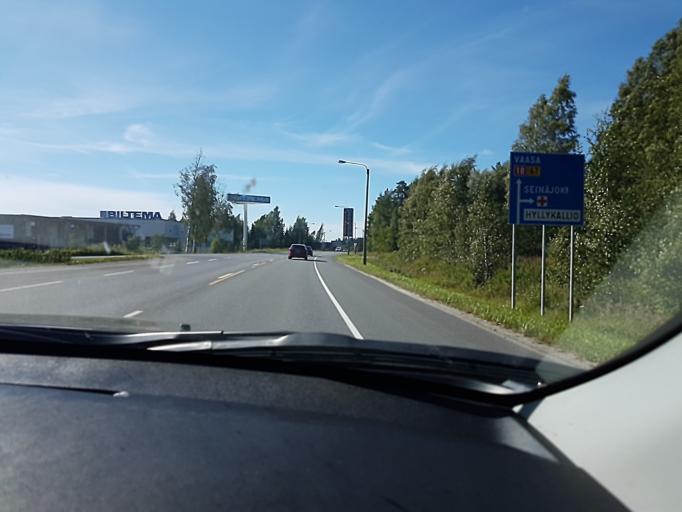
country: FI
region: Southern Ostrobothnia
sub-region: Seinaejoki
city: Nurmo
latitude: 62.7919
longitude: 22.8839
